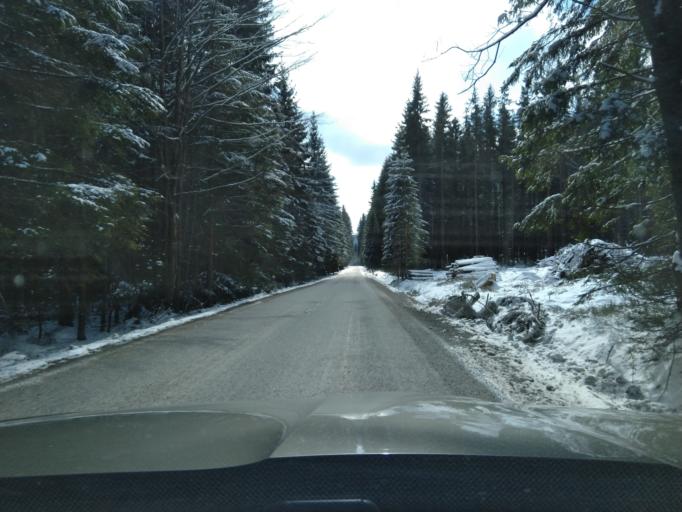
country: CZ
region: Jihocesky
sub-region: Okres Prachatice
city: Zdikov
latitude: 49.0523
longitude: 13.6604
